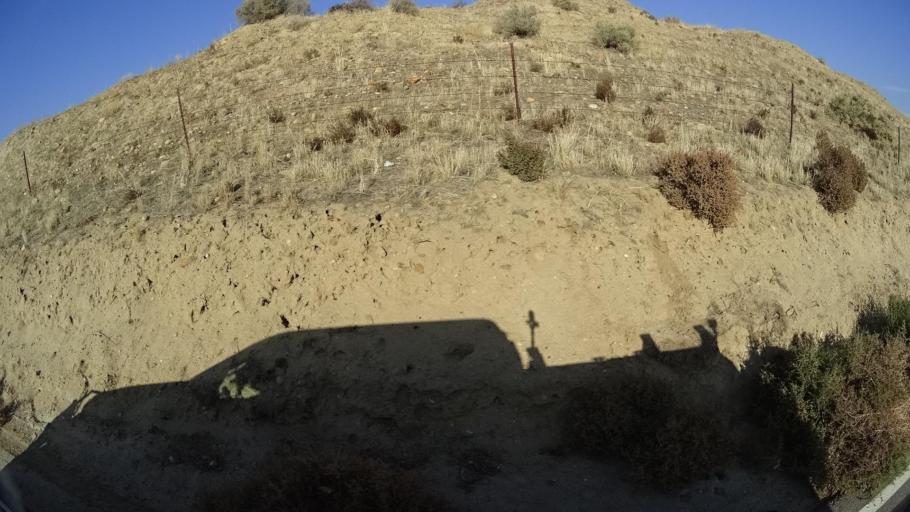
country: US
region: California
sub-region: Kern County
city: Oildale
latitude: 35.4501
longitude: -118.9237
